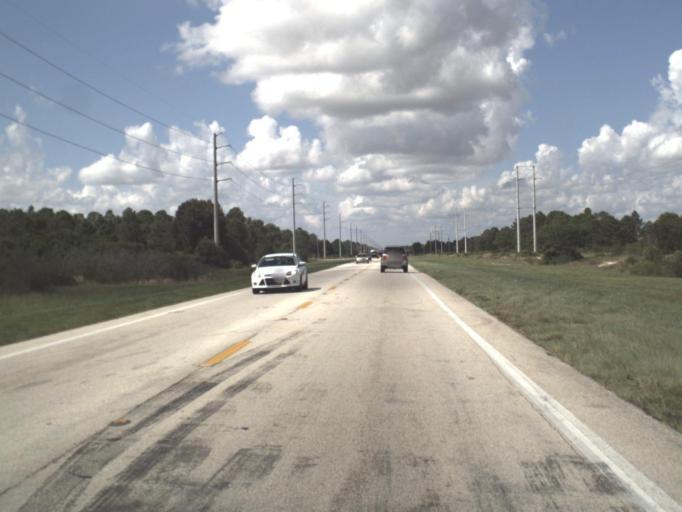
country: US
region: Florida
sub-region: Lee County
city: Gateway
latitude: 26.5777
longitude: -81.7044
